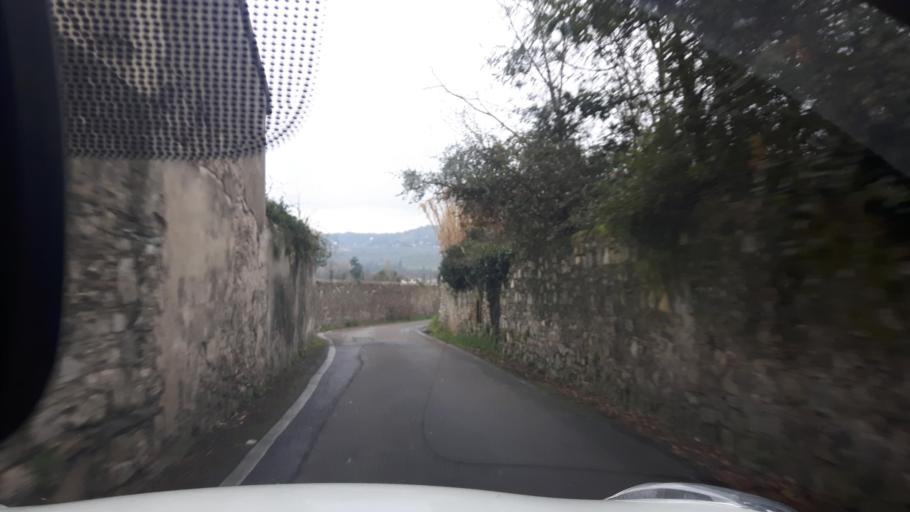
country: IT
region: Tuscany
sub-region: Province of Florence
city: Bagno a Ripoli
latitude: 43.7595
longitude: 11.3195
